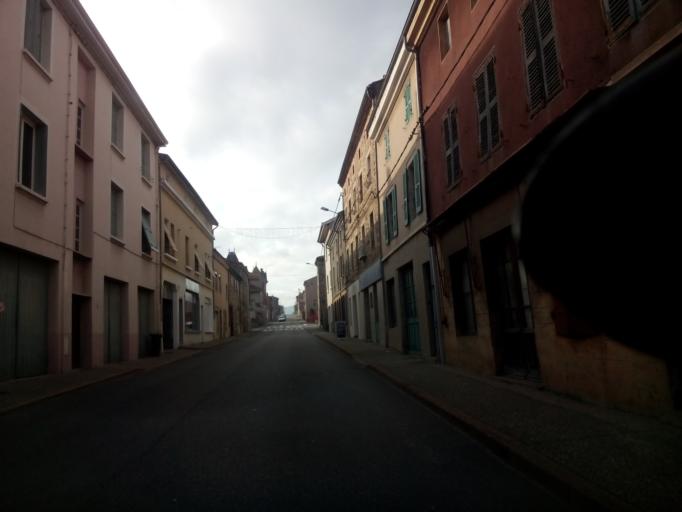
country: FR
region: Rhone-Alpes
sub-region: Departement de la Loire
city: Maclas
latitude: 45.3618
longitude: 4.6842
